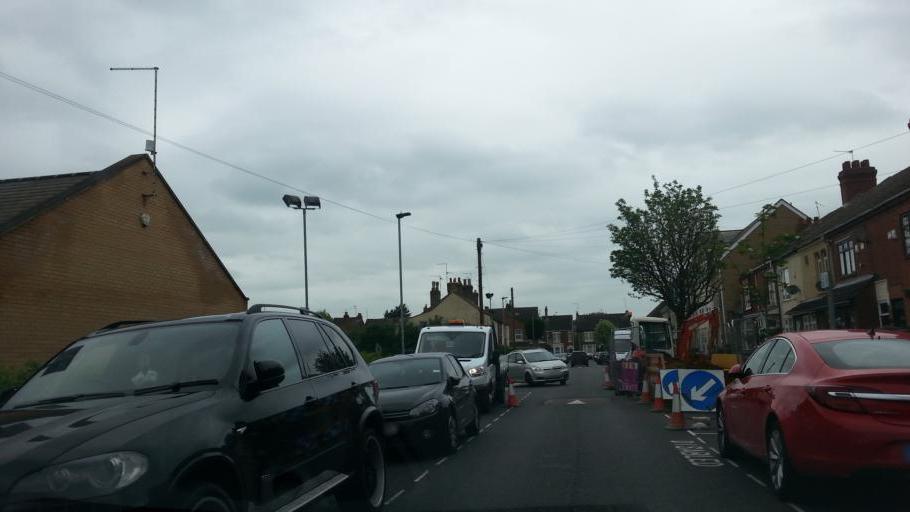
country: GB
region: England
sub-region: Peterborough
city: Peterborough
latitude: 52.5843
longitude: -0.2409
